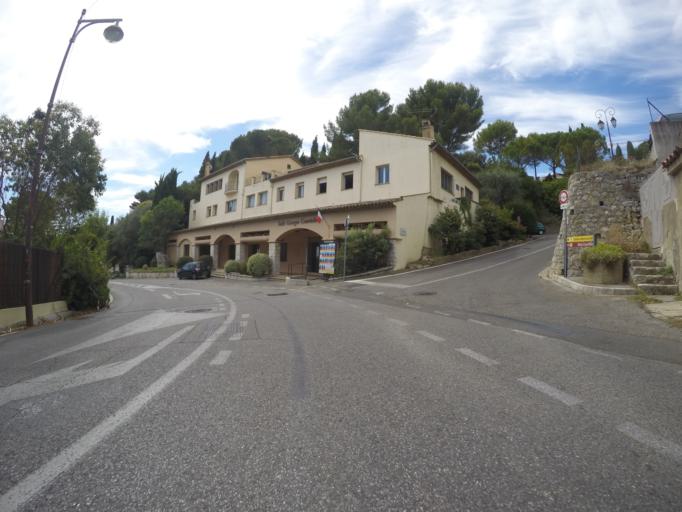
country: FR
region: Provence-Alpes-Cote d'Azur
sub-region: Departement des Alpes-Maritimes
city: Mougins
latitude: 43.5997
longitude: 6.9958
